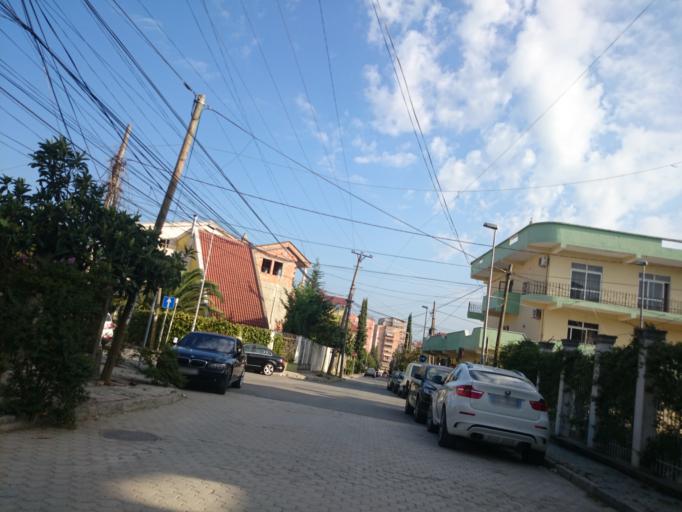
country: AL
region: Tirane
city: Tirana
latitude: 41.3156
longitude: 19.7995
